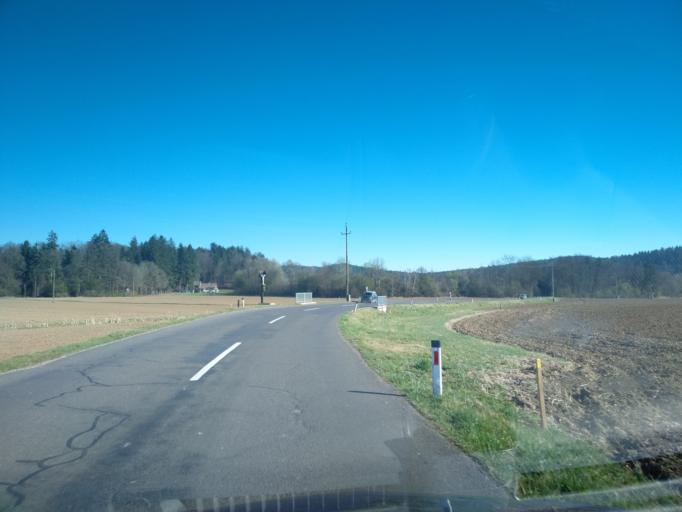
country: AT
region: Styria
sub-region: Politischer Bezirk Leibnitz
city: Weitendorf
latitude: 46.8992
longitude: 15.4409
